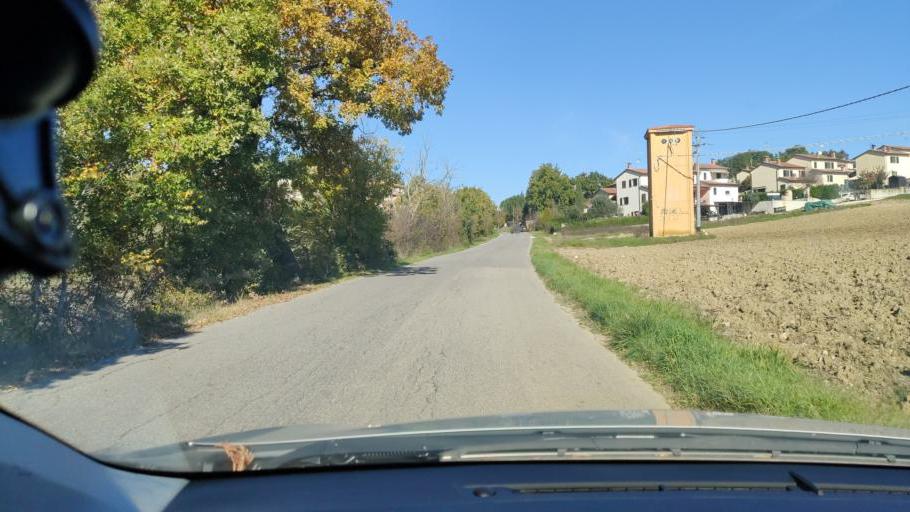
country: IT
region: Umbria
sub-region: Provincia di Terni
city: Amelia
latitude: 42.5952
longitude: 12.4368
